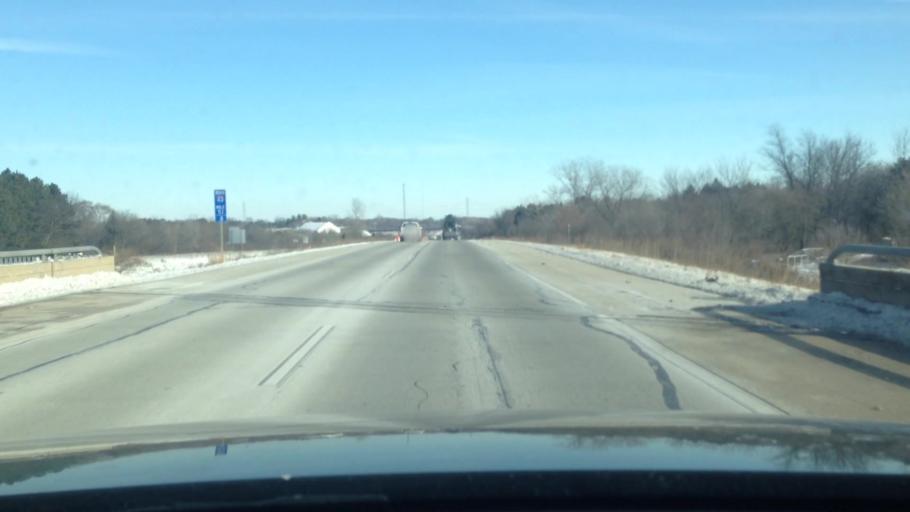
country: US
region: Wisconsin
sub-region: Waukesha County
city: Big Bend
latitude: 42.9189
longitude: -88.1989
